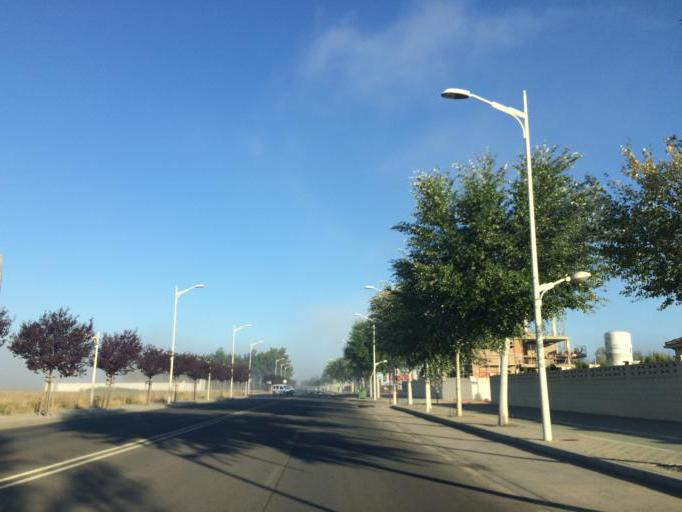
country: ES
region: Castille-La Mancha
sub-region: Provincia de Albacete
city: Albacete
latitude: 39.0033
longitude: -1.8813
